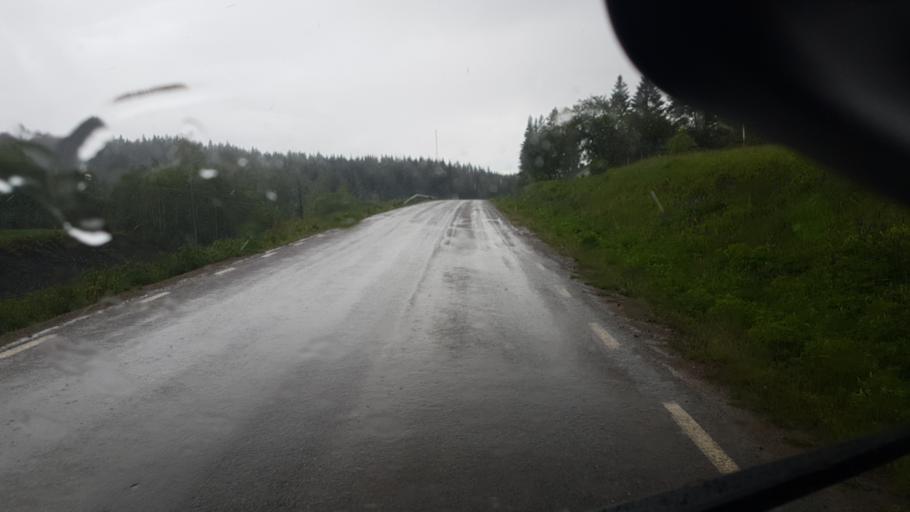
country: SE
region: Vaermland
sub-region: Eda Kommun
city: Amotfors
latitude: 59.6981
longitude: 12.4620
